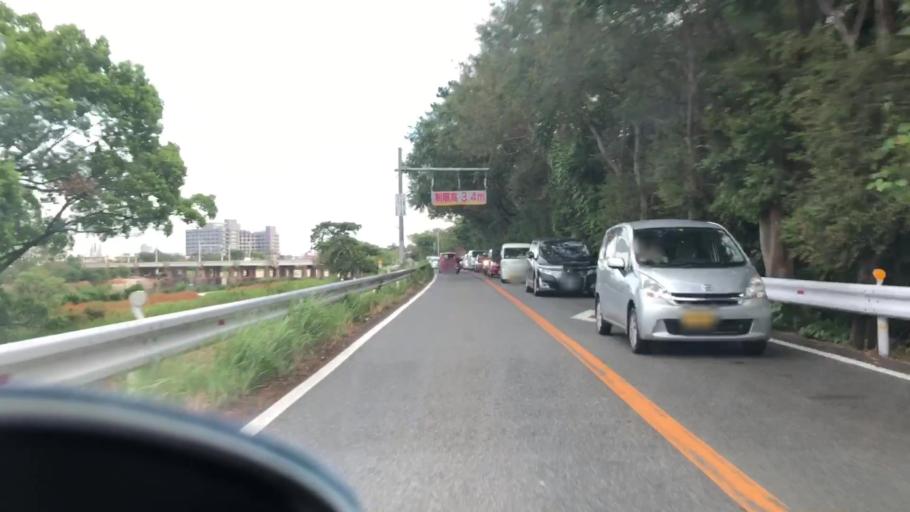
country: JP
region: Hyogo
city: Amagasaki
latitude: 34.7412
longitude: 135.3776
